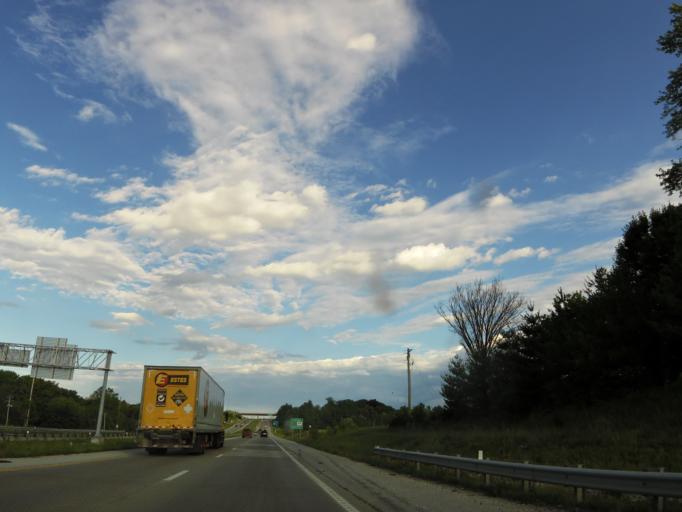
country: US
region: Missouri
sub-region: Saint Charles County
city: Lake Saint Louis
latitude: 38.7863
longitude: -90.8036
